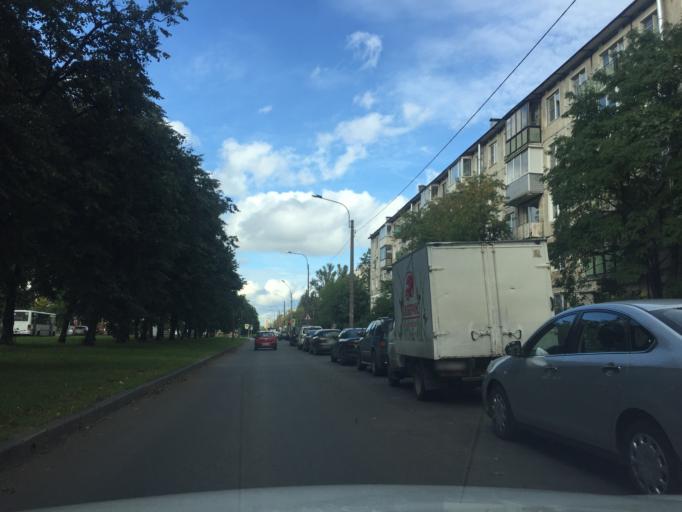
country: RU
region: St.-Petersburg
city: Kupchino
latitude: 59.8571
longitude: 30.3378
